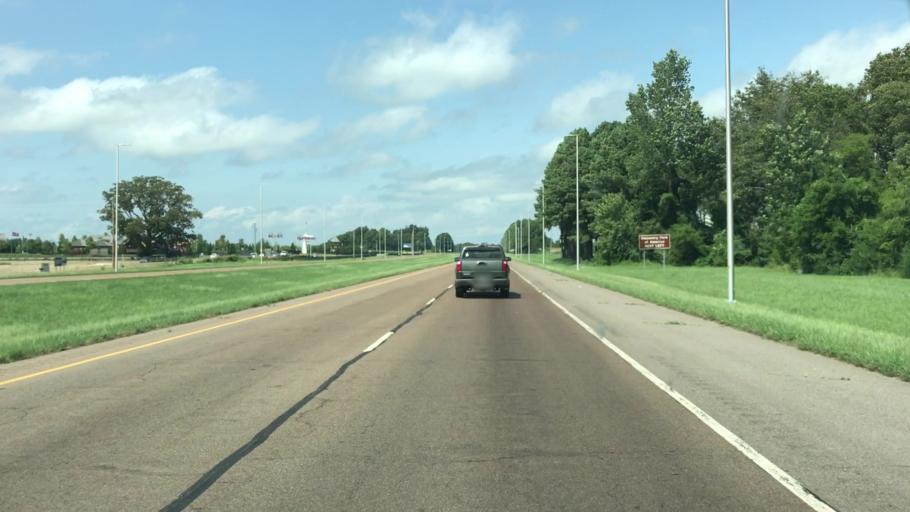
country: US
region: Tennessee
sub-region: Obion County
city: Union City
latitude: 36.4339
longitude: -89.0671
